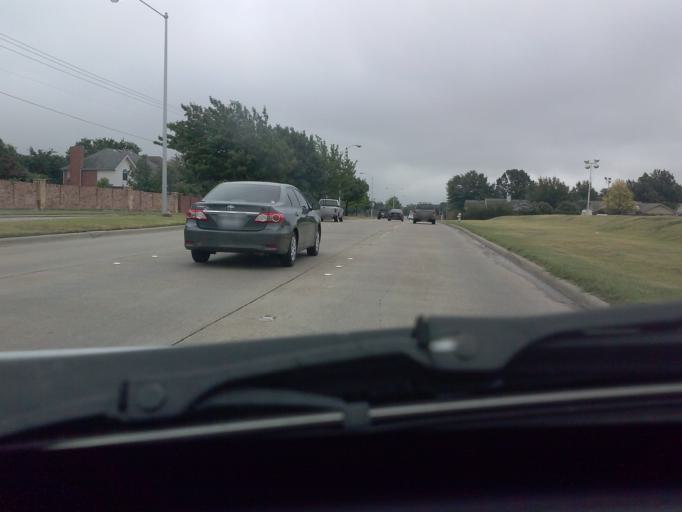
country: US
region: Texas
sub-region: Collin County
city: Plano
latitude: 33.0715
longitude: -96.7349
